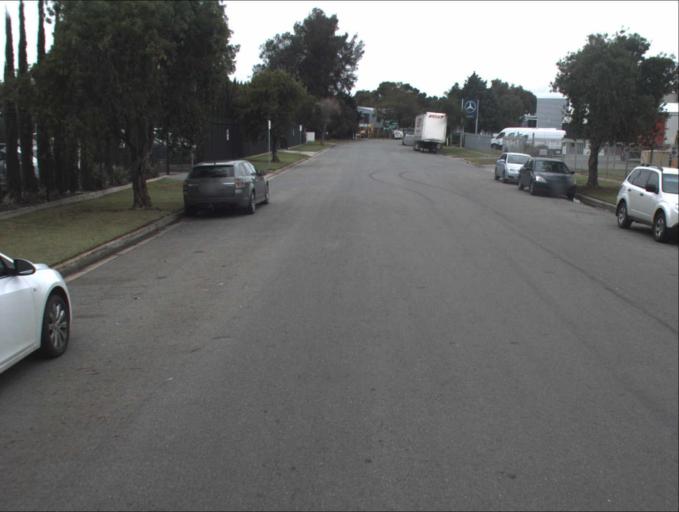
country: AU
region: South Australia
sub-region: Port Adelaide Enfield
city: Blair Athol
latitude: -34.8636
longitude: 138.5706
